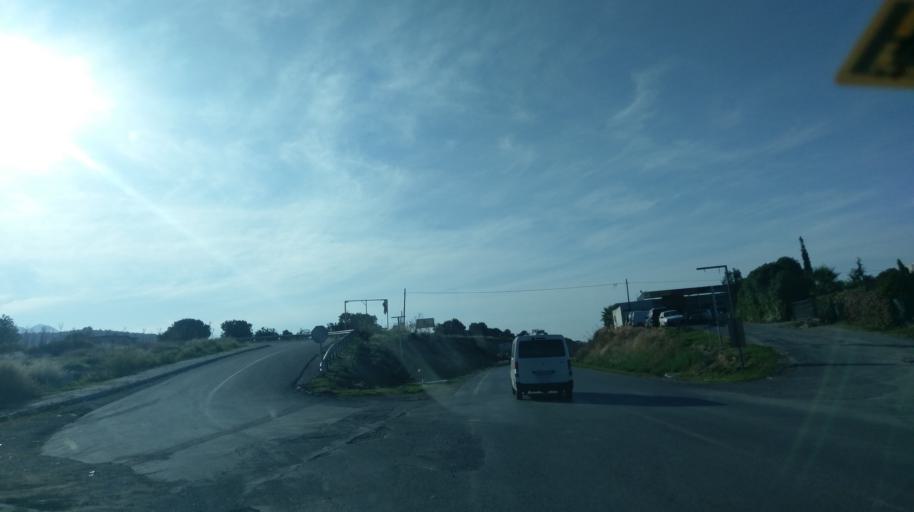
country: CY
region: Ammochostos
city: Lefkonoiko
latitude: 35.3526
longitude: 33.6274
